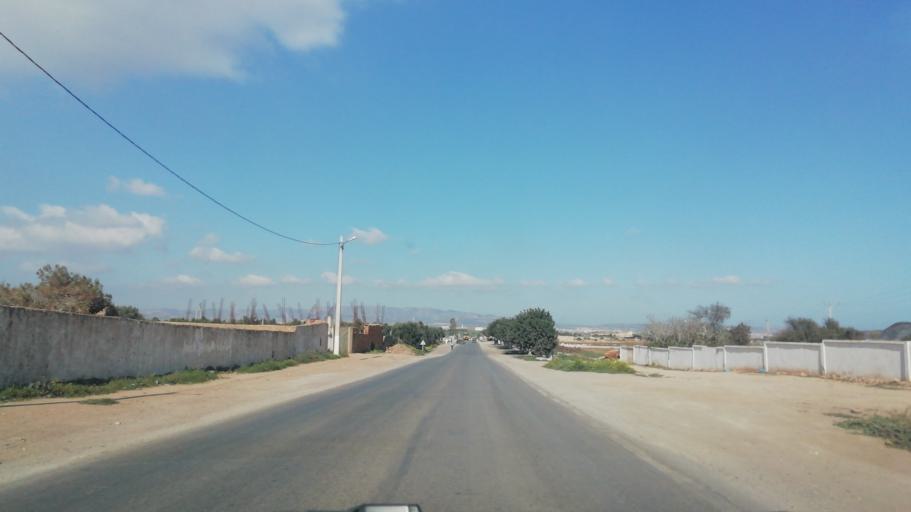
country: DZ
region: Oran
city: Ain el Bya
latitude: 35.7793
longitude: -0.2805
